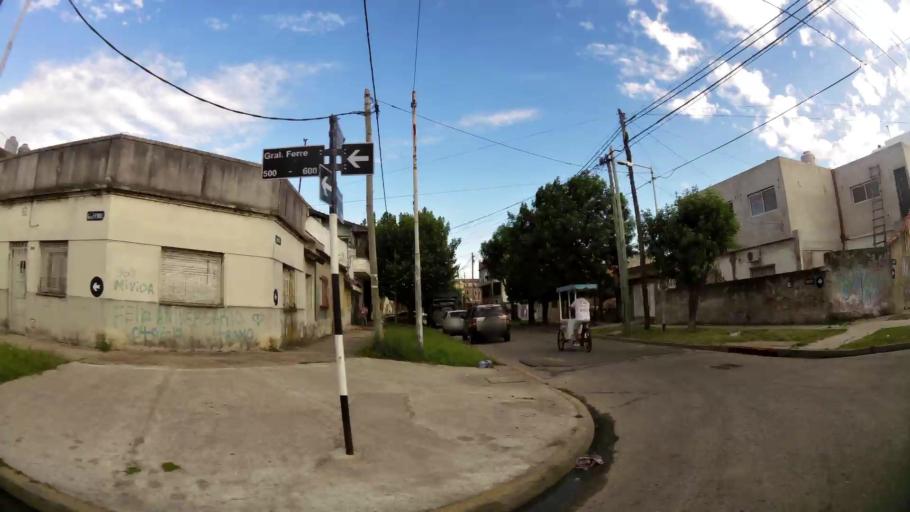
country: AR
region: Buenos Aires
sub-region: Partido de Avellaneda
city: Avellaneda
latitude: -34.6860
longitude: -58.3509
